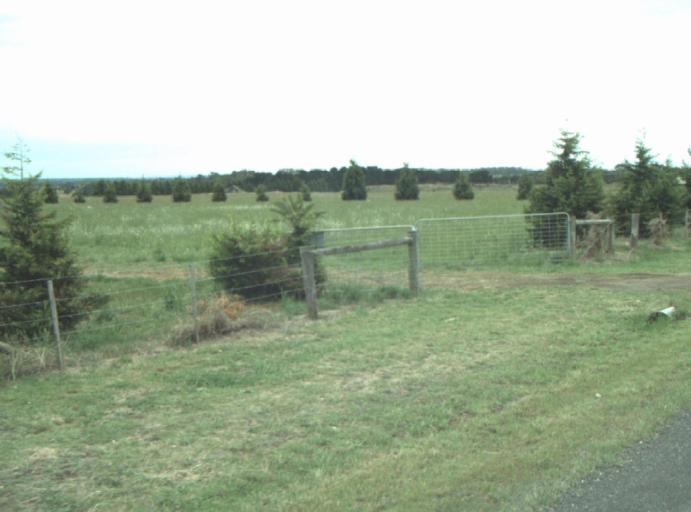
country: AU
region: Victoria
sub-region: Greater Geelong
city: Leopold
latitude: -38.2086
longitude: 144.4511
